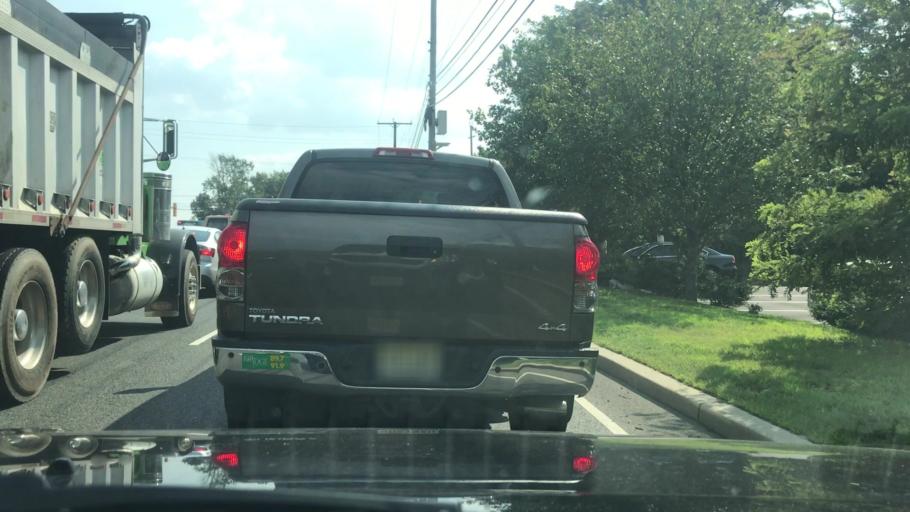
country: US
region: New Jersey
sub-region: Monmouth County
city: Farmingdale
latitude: 40.2202
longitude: -74.1239
